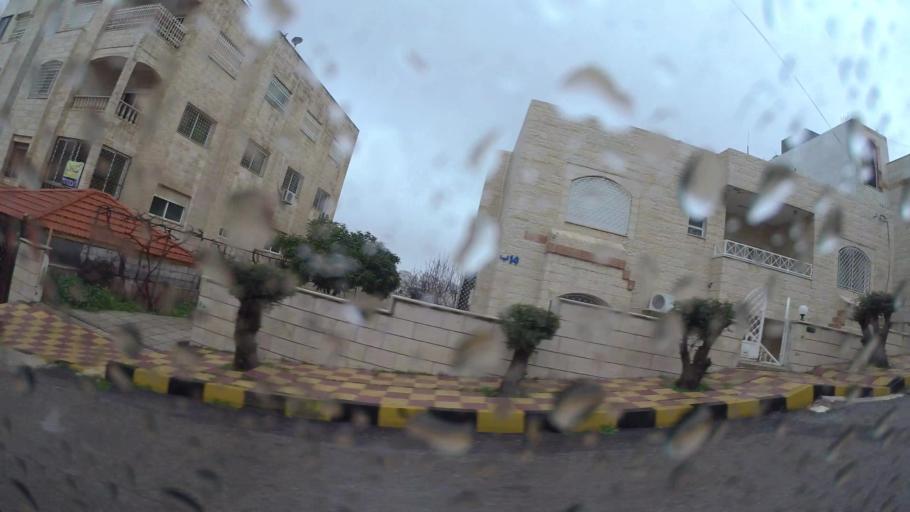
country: JO
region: Amman
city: Al Jubayhah
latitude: 32.0145
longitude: 35.8817
